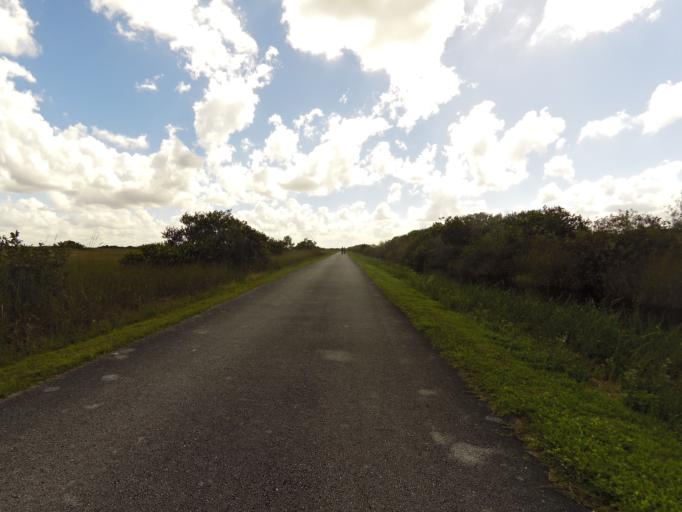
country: US
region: Florida
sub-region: Miami-Dade County
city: The Hammocks
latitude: 25.7215
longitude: -80.7667
